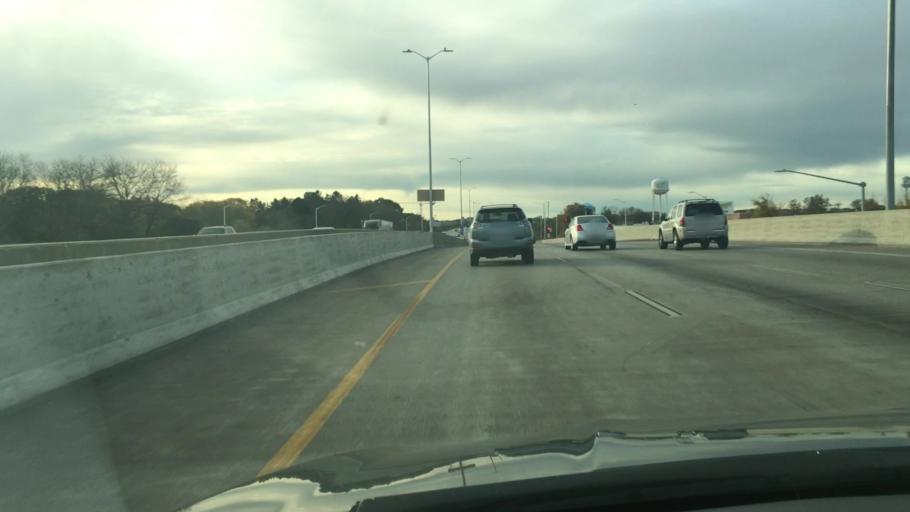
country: US
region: Wisconsin
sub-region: Waukesha County
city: Butler
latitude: 43.0891
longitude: -88.0581
